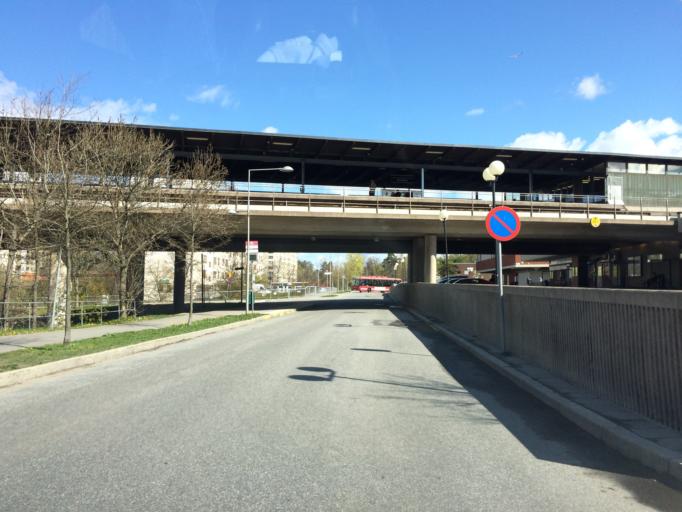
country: SE
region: Stockholm
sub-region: Huddinge Kommun
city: Segeltorp
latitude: 59.2943
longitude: 17.9330
